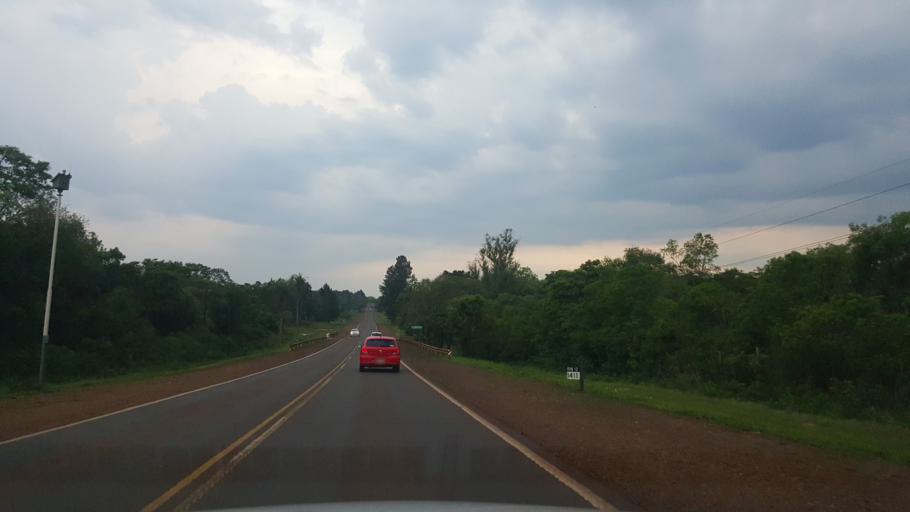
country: AR
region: Misiones
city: Gobernador Roca
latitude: -27.1754
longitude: -55.4523
